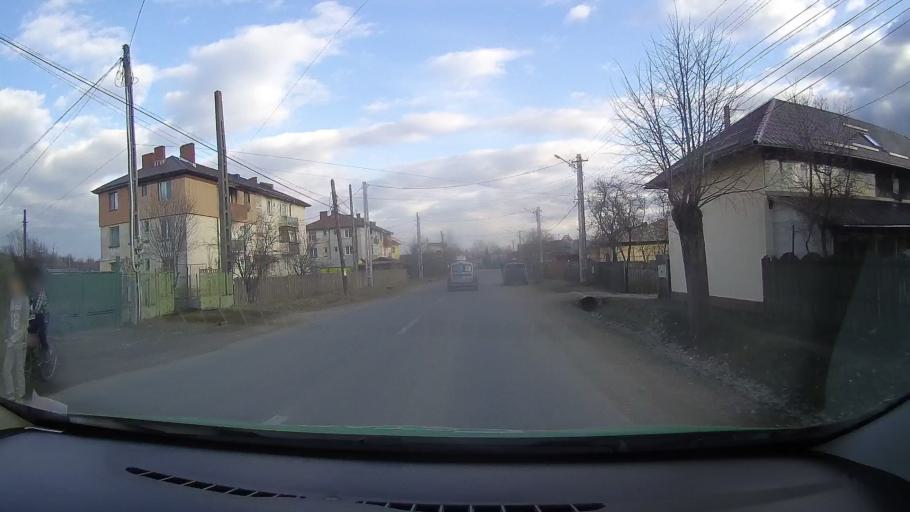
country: RO
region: Dambovita
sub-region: Comuna Gura Ocnitei
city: Gura Ocnitei
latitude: 44.9452
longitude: 25.5610
